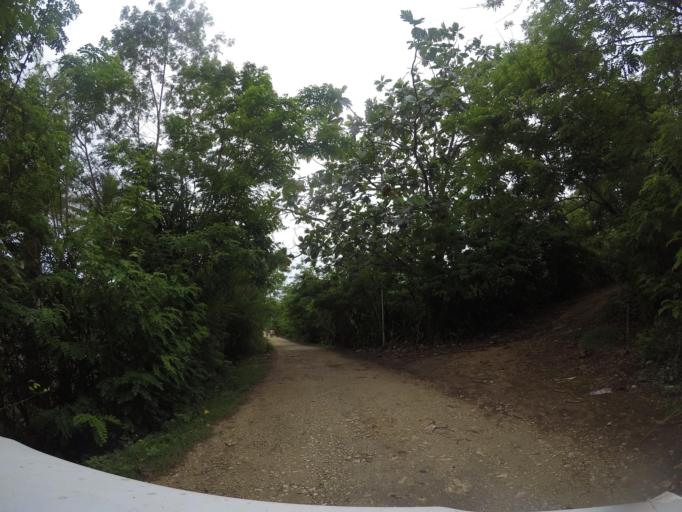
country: TL
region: Lautem
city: Lospalos
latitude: -8.5376
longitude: 126.9962
